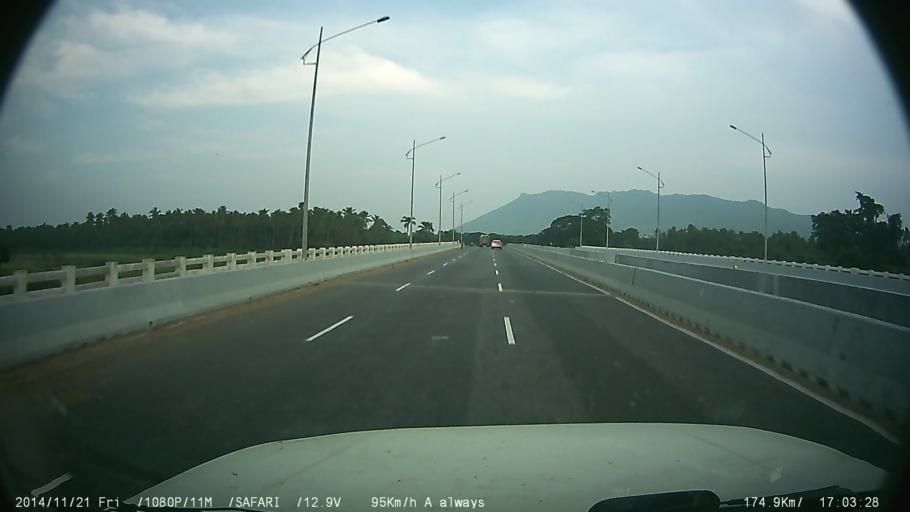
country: IN
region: Tamil Nadu
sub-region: Vellore
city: Pallikondai
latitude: 12.8954
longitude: 78.9149
